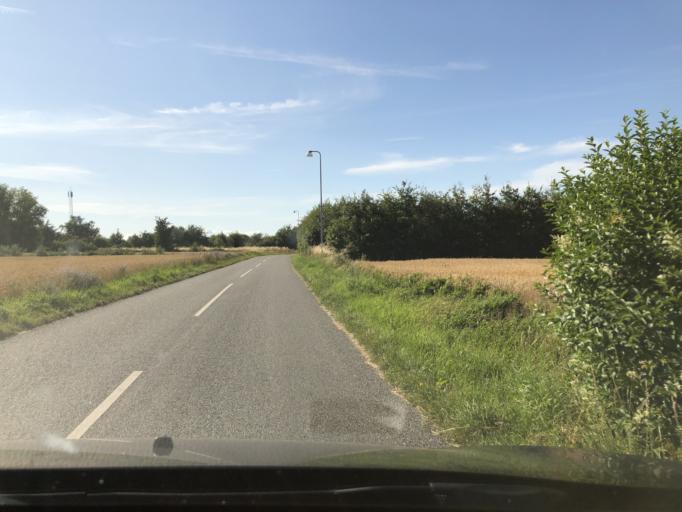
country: DK
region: South Denmark
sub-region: AEro Kommune
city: Marstal
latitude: 54.8682
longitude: 10.4987
